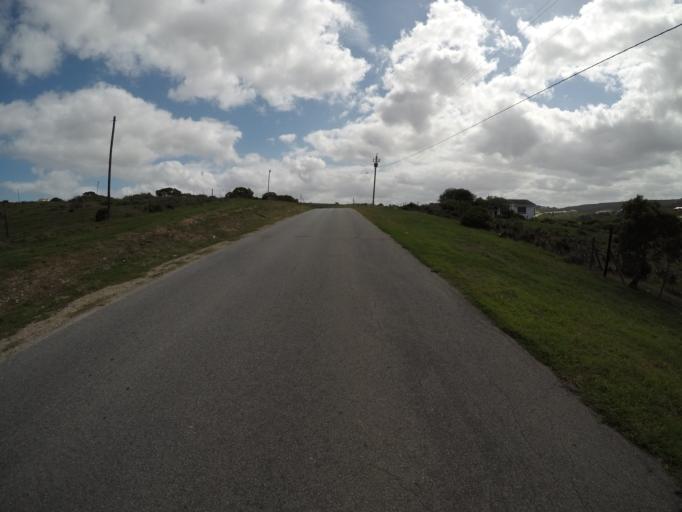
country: ZA
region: Western Cape
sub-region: Eden District Municipality
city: Mossel Bay
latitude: -34.1450
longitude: 22.0906
